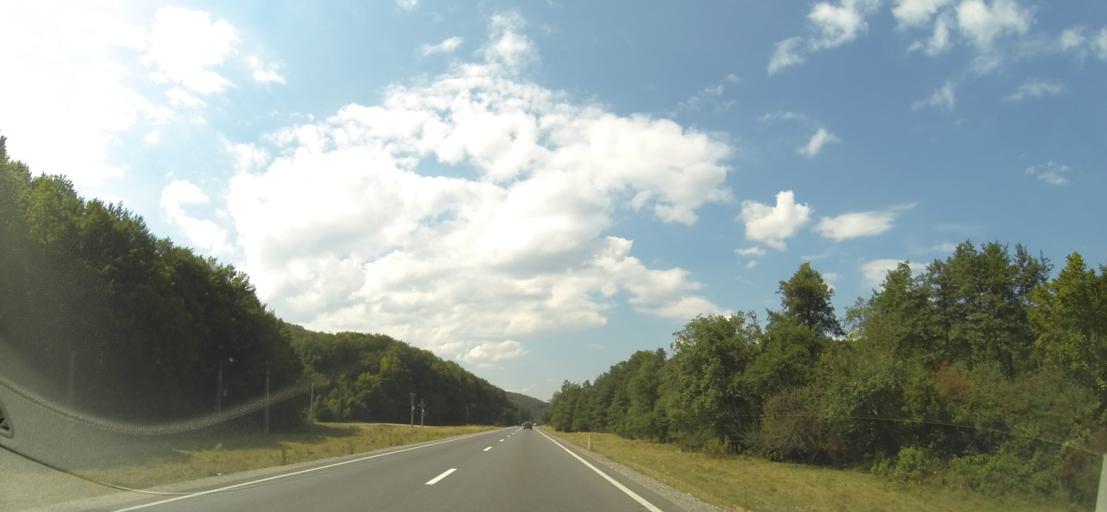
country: RO
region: Brasov
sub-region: Comuna Sinca Veche
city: Persani
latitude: 45.7549
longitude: 25.2502
